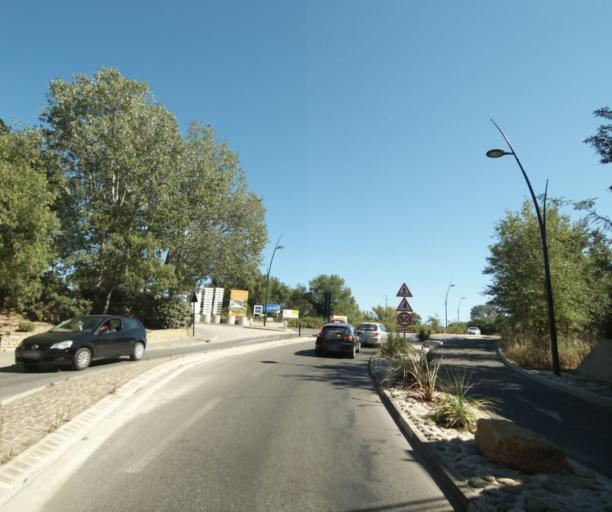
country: FR
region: Provence-Alpes-Cote d'Azur
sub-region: Departement du Var
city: La Garde
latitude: 43.1193
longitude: 6.0111
